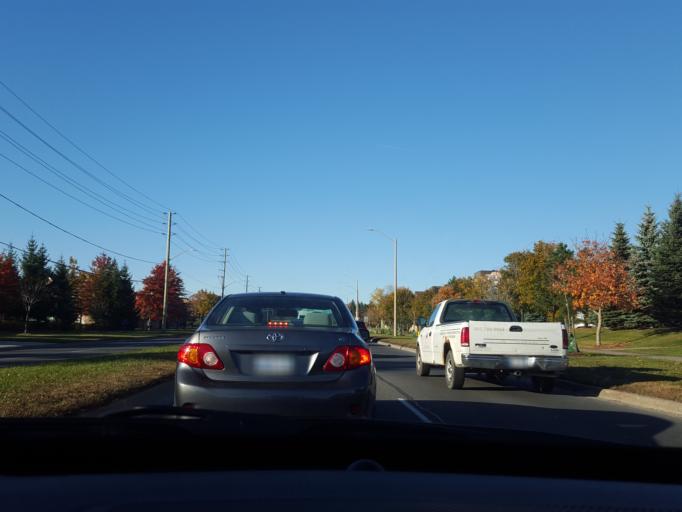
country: CA
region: Ontario
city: Markham
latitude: 43.8747
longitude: -79.2863
